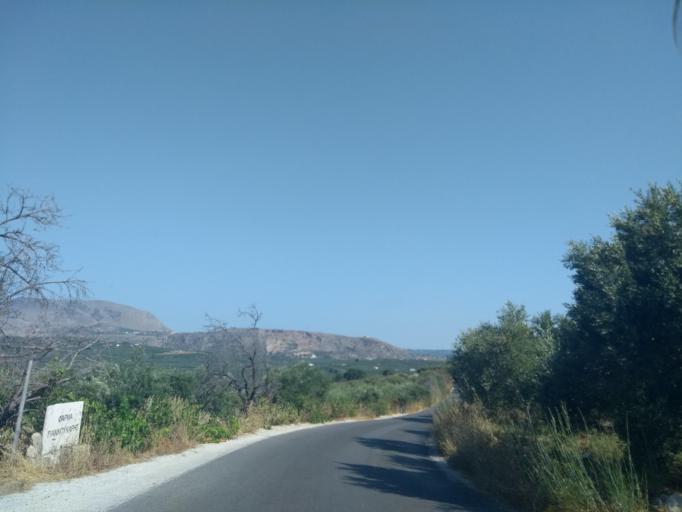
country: GR
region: Crete
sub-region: Nomos Chanias
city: Kalivai
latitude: 35.4365
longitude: 24.1737
